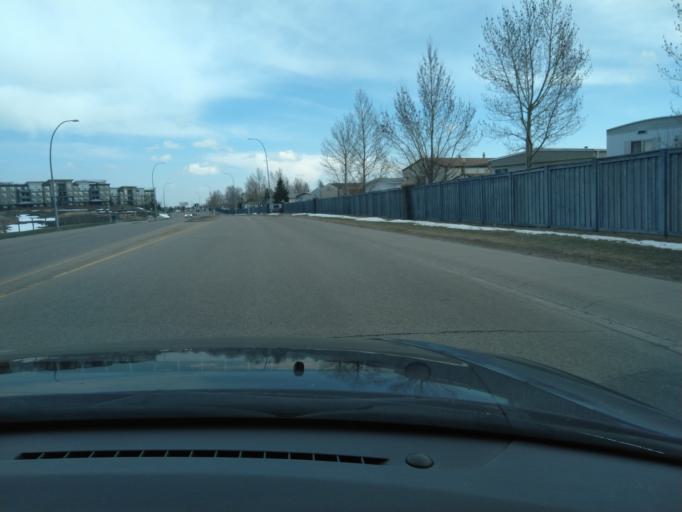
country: CA
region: Alberta
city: Calgary
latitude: 51.1292
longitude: -114.2152
